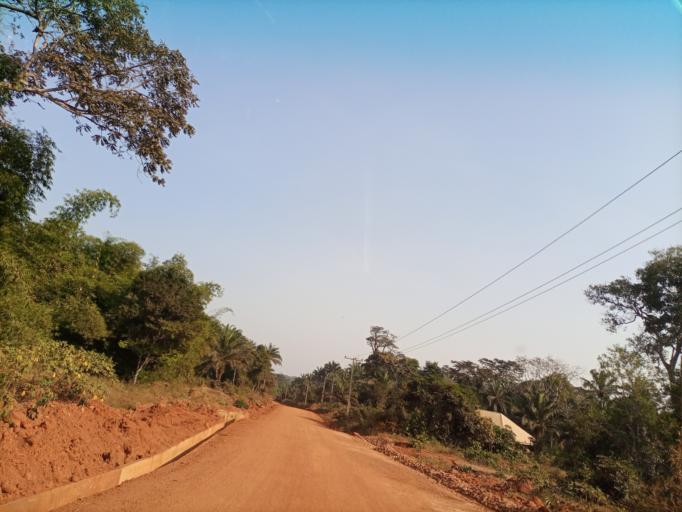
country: NG
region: Enugu
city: Opi
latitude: 6.7609
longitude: 7.3984
